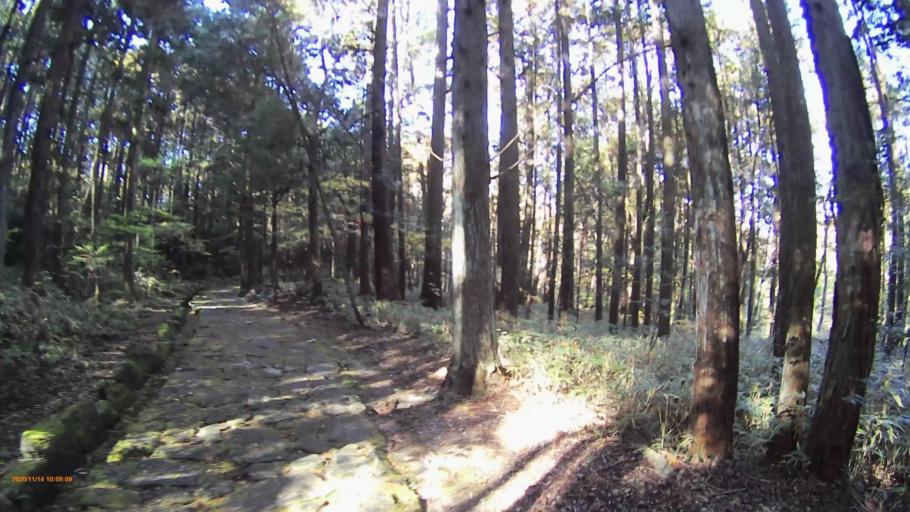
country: JP
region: Gifu
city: Nakatsugawa
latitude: 35.5132
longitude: 137.5453
